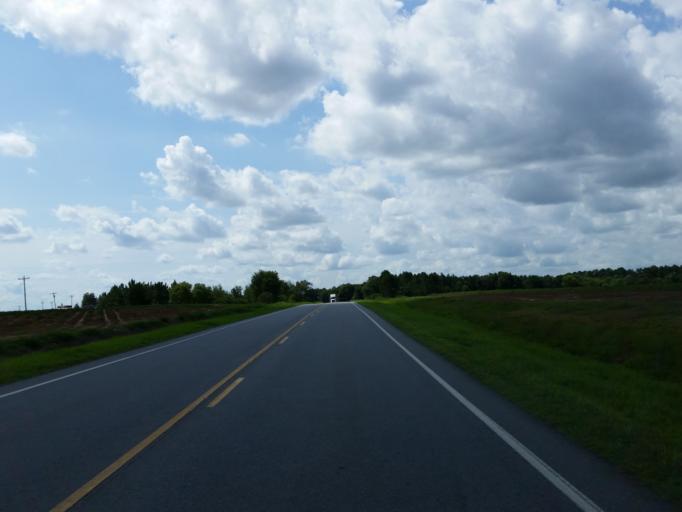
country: US
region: Georgia
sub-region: Turner County
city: Ashburn
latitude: 31.6610
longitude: -83.5999
